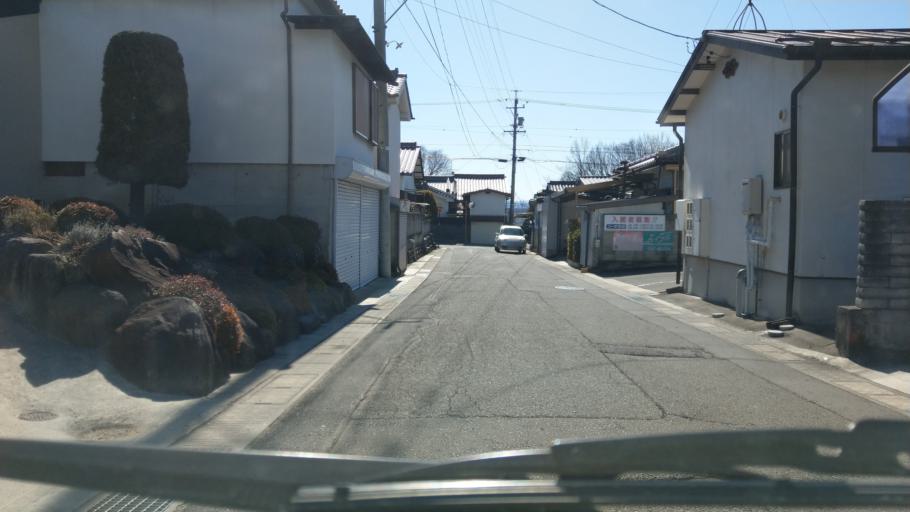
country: JP
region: Nagano
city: Komoro
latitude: 36.3321
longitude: 138.4119
